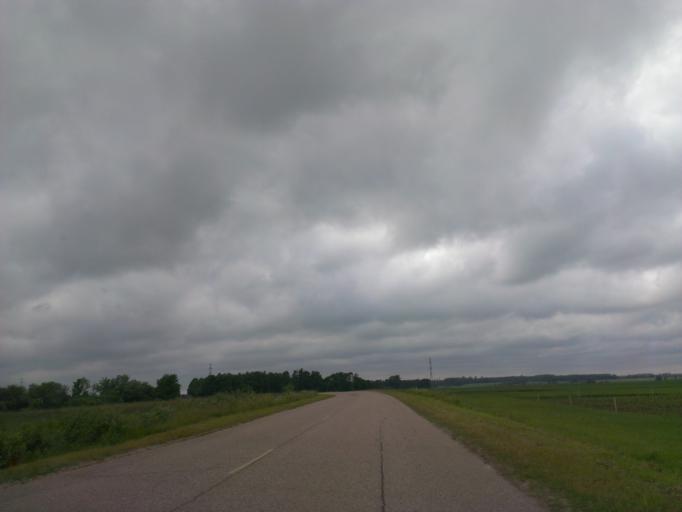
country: LV
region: Aizpute
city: Aizpute
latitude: 56.7201
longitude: 21.4465
